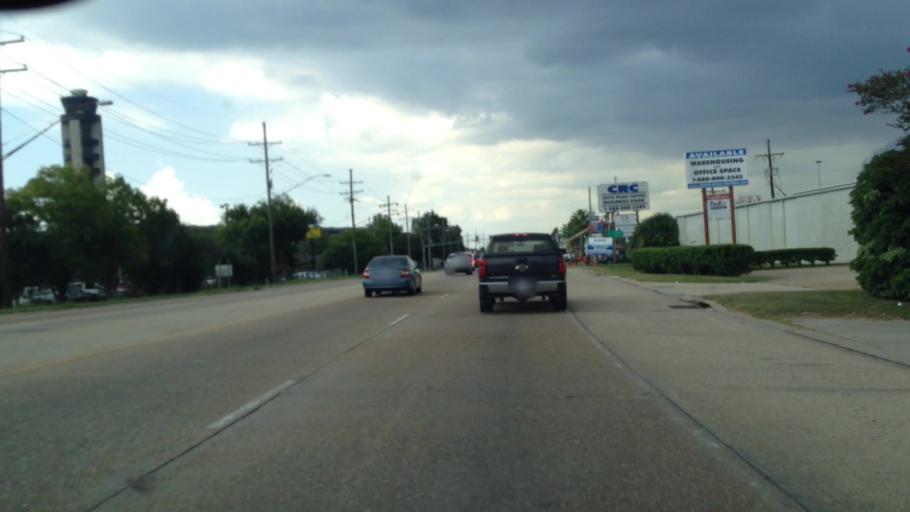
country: US
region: Louisiana
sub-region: Jefferson Parish
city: Kenner
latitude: 29.9833
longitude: -90.2624
